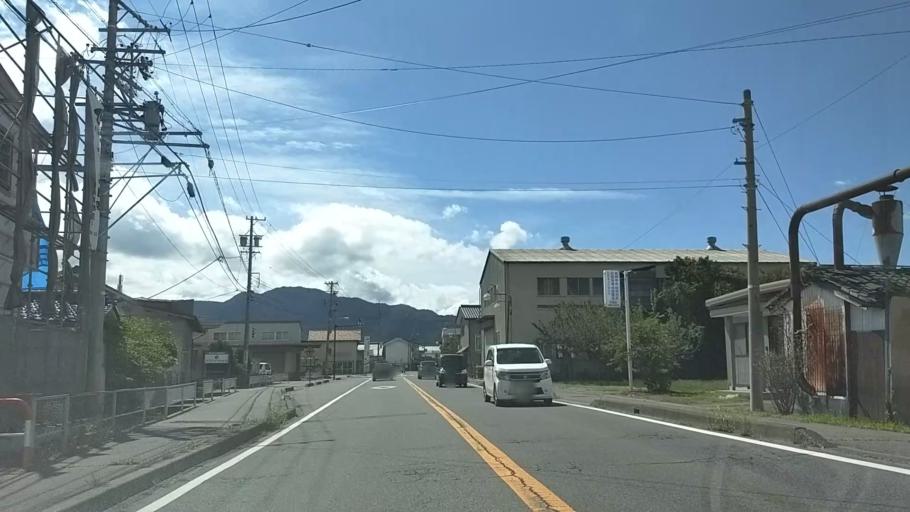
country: JP
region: Nagano
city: Suzaka
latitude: 36.6278
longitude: 138.2601
